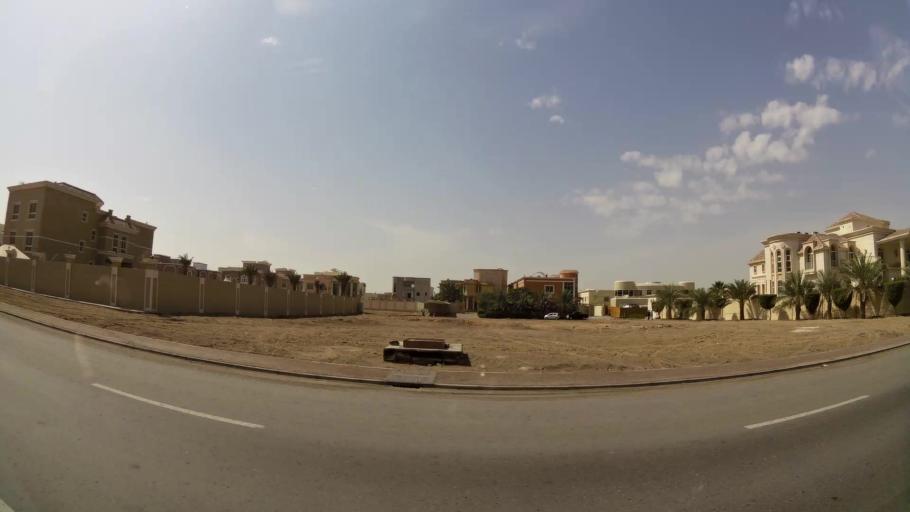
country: AE
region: Abu Dhabi
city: Abu Dhabi
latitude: 24.3200
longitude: 54.5745
